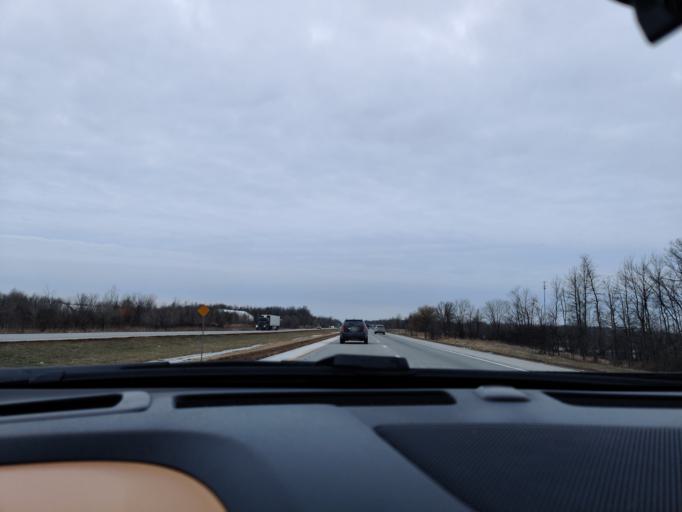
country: US
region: New York
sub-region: St. Lawrence County
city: Ogdensburg
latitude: 44.8644
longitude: -75.3172
